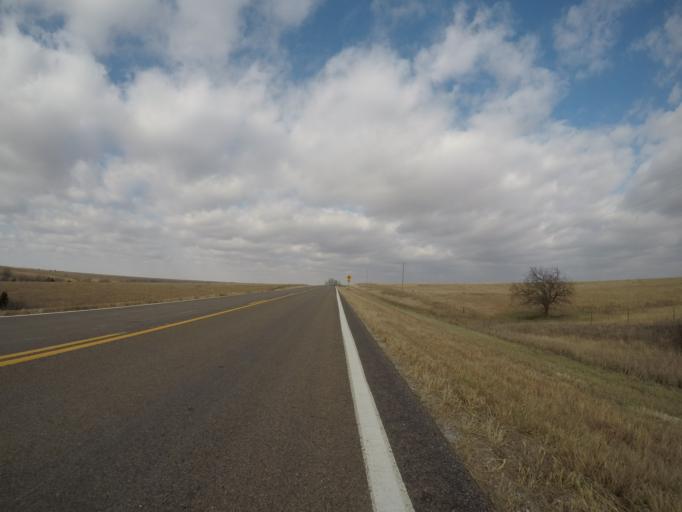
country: US
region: Kansas
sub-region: Wabaunsee County
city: Alma
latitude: 38.8637
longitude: -96.3725
